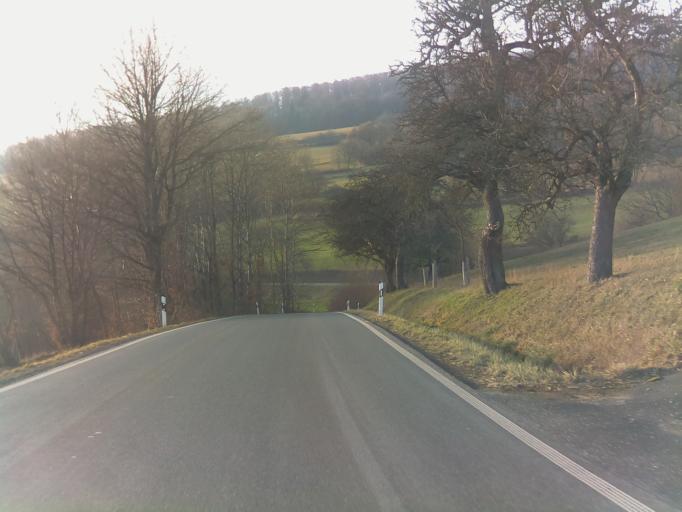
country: DE
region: Bavaria
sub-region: Regierungsbezirk Unterfranken
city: Zeitlofs
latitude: 50.3088
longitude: 9.7149
